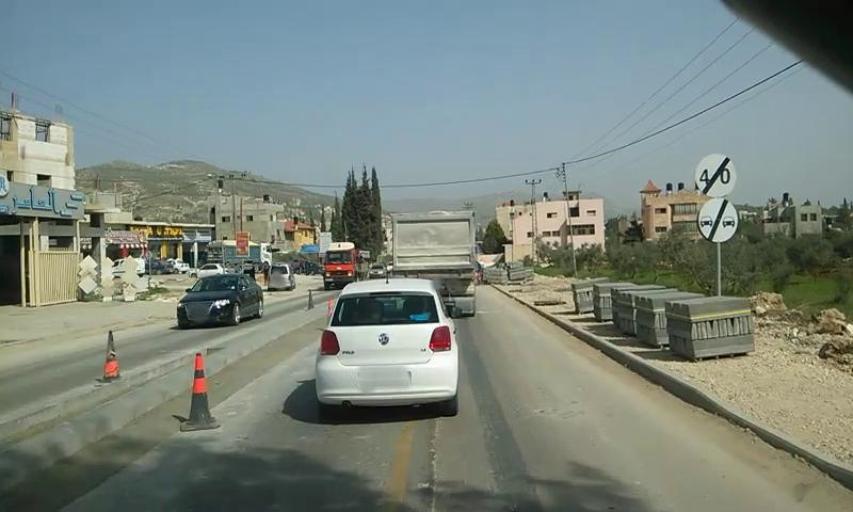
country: PS
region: West Bank
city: Huwwarah
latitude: 32.1391
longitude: 35.2580
